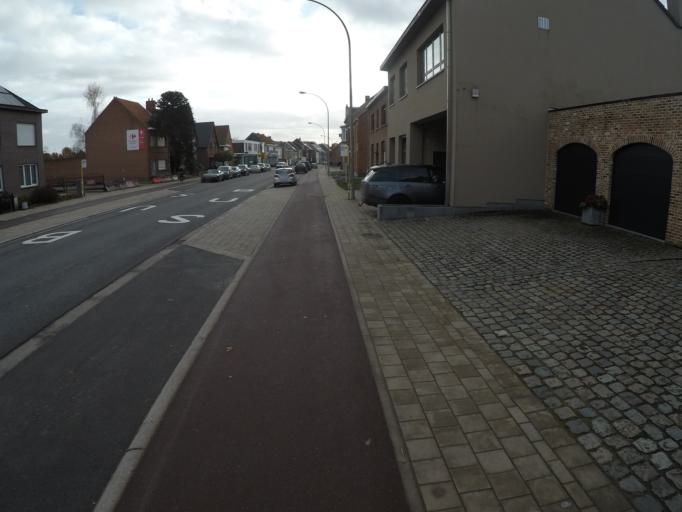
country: BE
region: Flanders
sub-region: Provincie Vlaams-Brabant
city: Londerzeel
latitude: 51.0142
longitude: 4.2954
